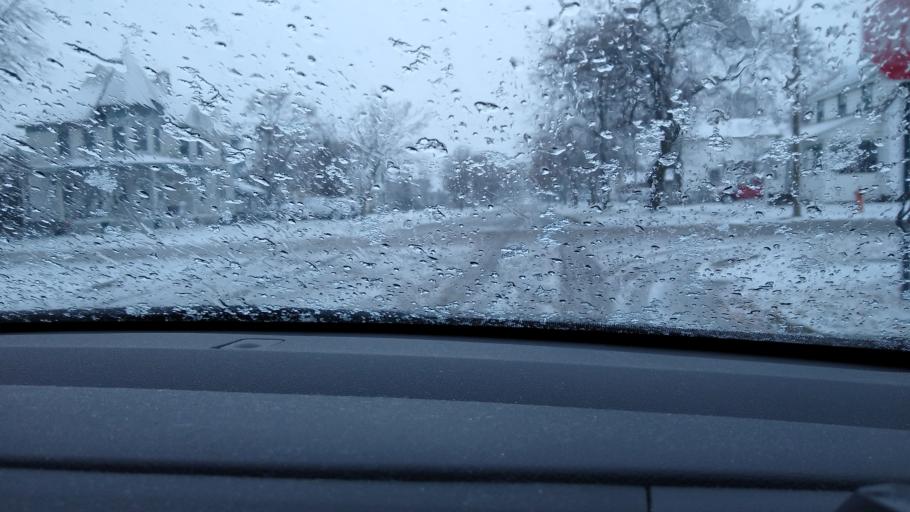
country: US
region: Michigan
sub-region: Delta County
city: Escanaba
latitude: 45.7396
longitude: -87.0610
